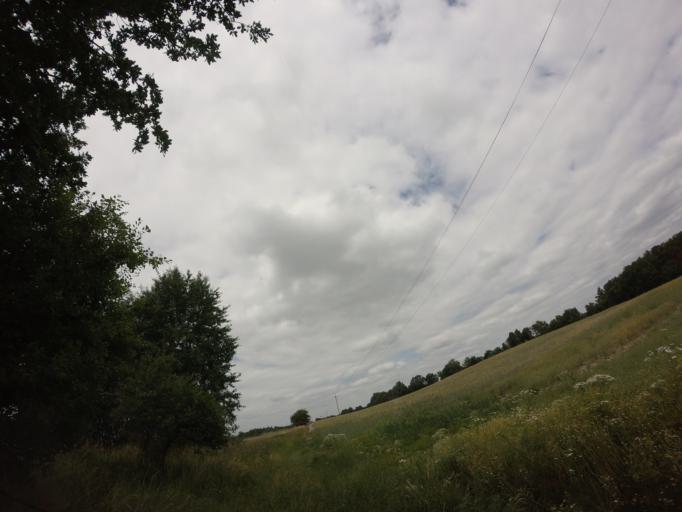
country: PL
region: West Pomeranian Voivodeship
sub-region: Powiat choszczenski
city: Krzecin
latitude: 53.0683
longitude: 15.5309
